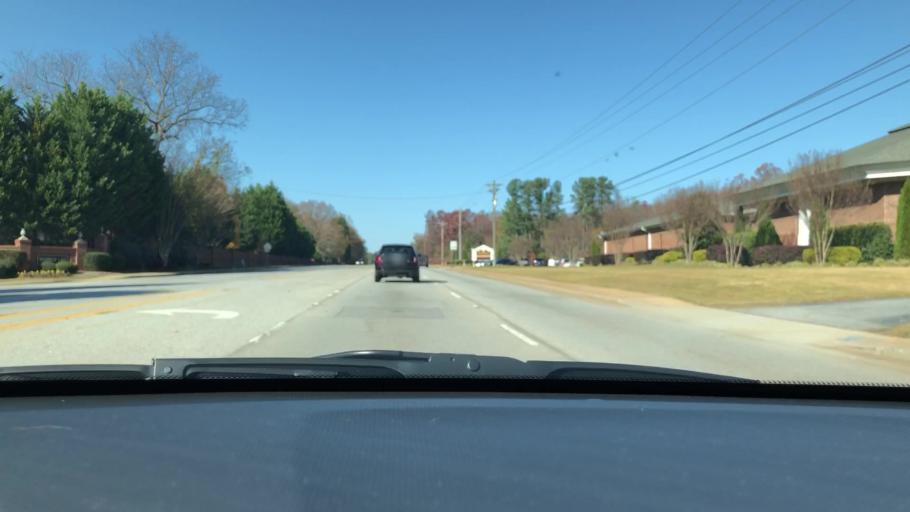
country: US
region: South Carolina
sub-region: Greenville County
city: Five Forks
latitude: 34.8091
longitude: -82.2370
